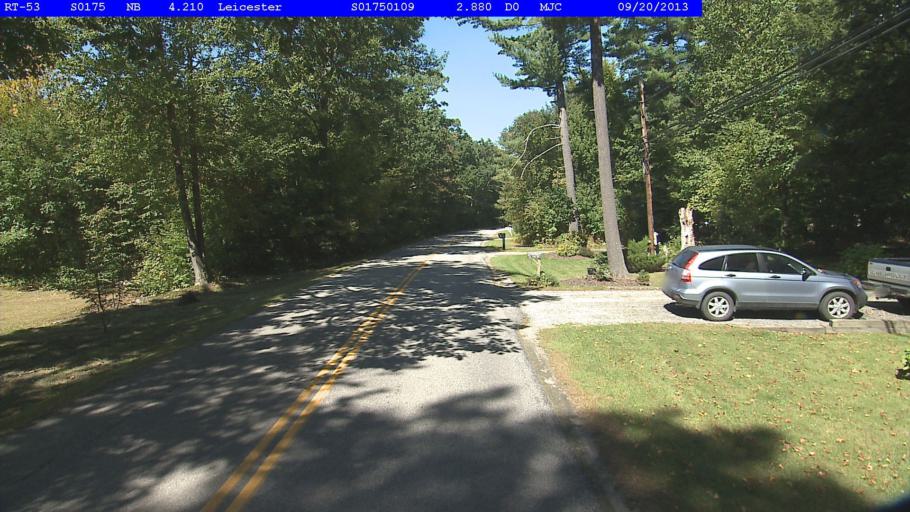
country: US
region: Vermont
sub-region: Rutland County
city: Brandon
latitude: 43.8841
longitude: -73.0640
